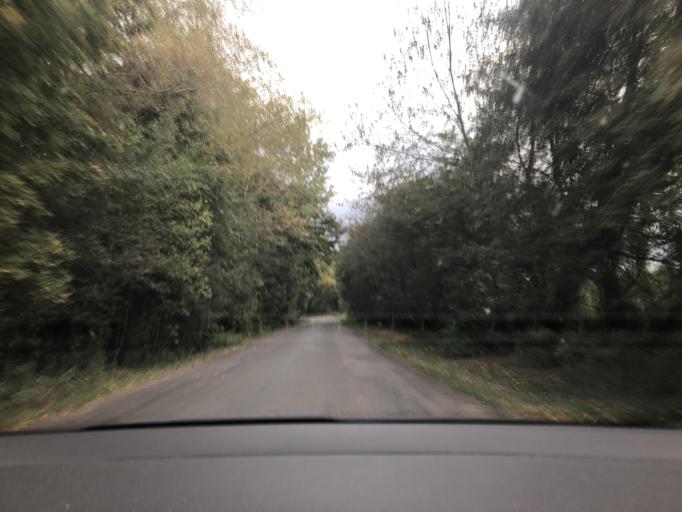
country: CZ
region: Pardubicky
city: Chvaletice
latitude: 50.0498
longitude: 15.4280
